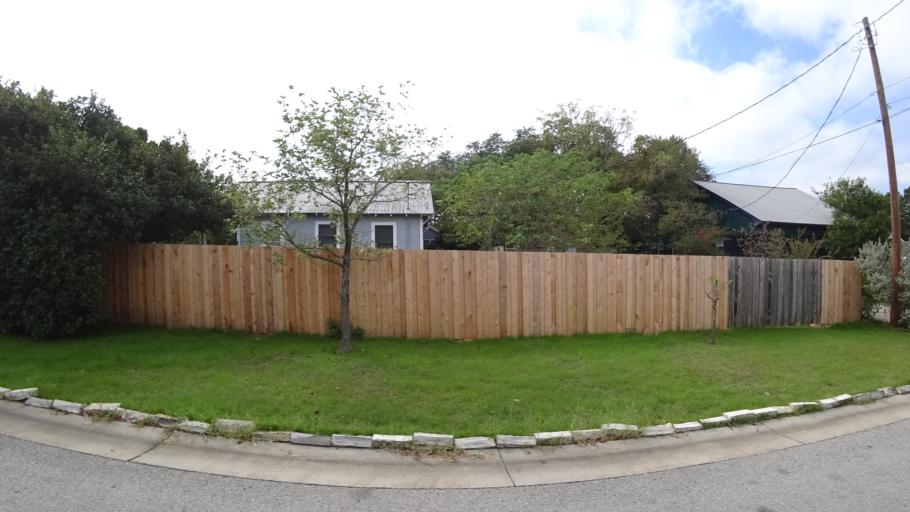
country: US
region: Texas
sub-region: Travis County
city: Shady Hollow
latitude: 30.2035
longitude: -97.8353
